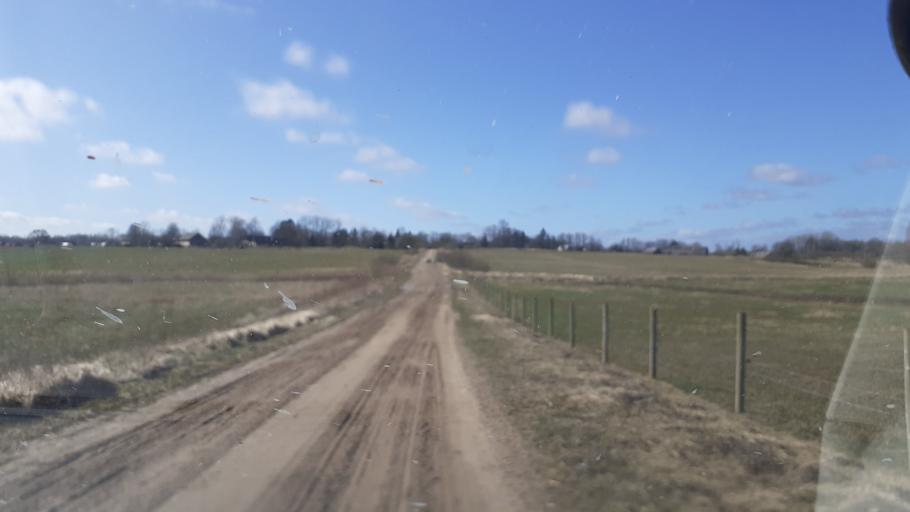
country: LV
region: Kuldigas Rajons
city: Kuldiga
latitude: 56.9335
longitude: 22.1675
